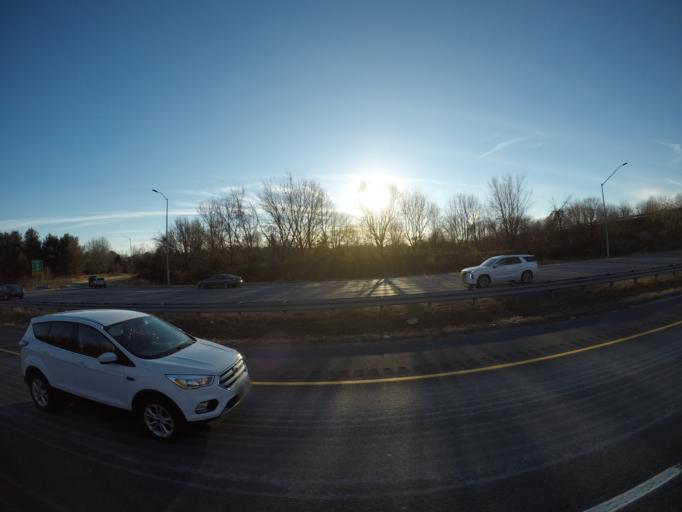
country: US
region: Maryland
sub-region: Howard County
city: Columbia
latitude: 39.2469
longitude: -76.8164
